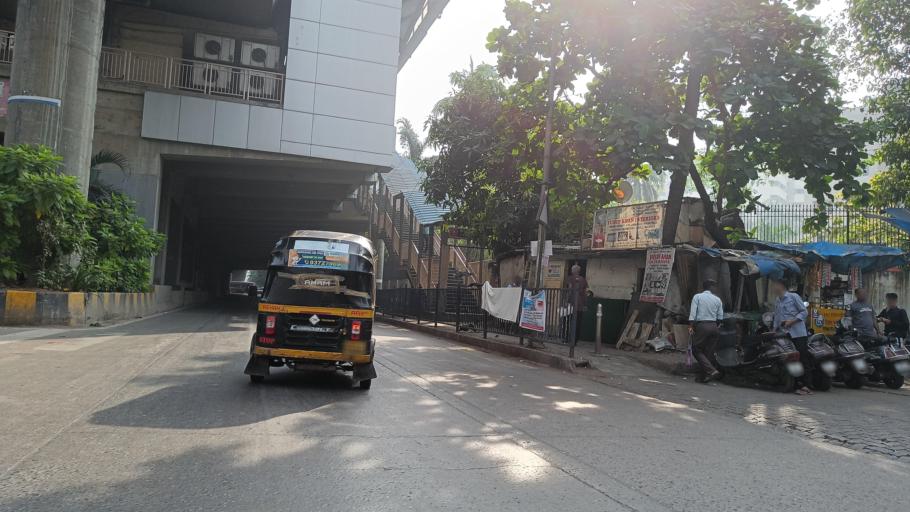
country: IN
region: Maharashtra
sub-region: Mumbai Suburban
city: Powai
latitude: 19.1285
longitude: 72.8293
